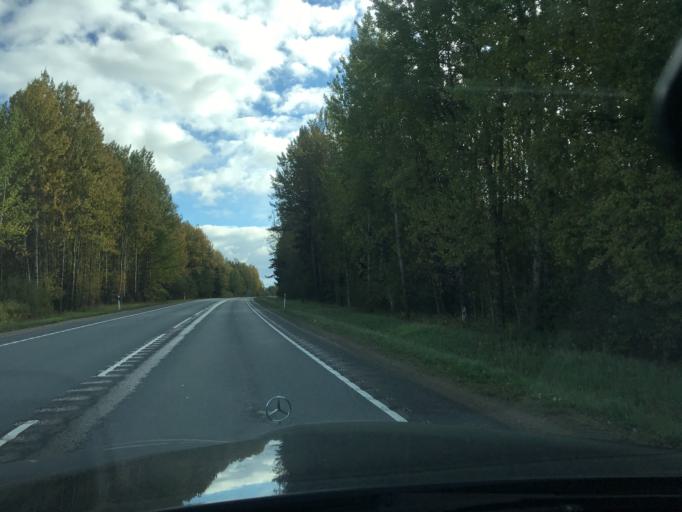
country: EE
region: Vorumaa
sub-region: Voru linn
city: Voru
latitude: 57.8645
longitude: 26.9614
